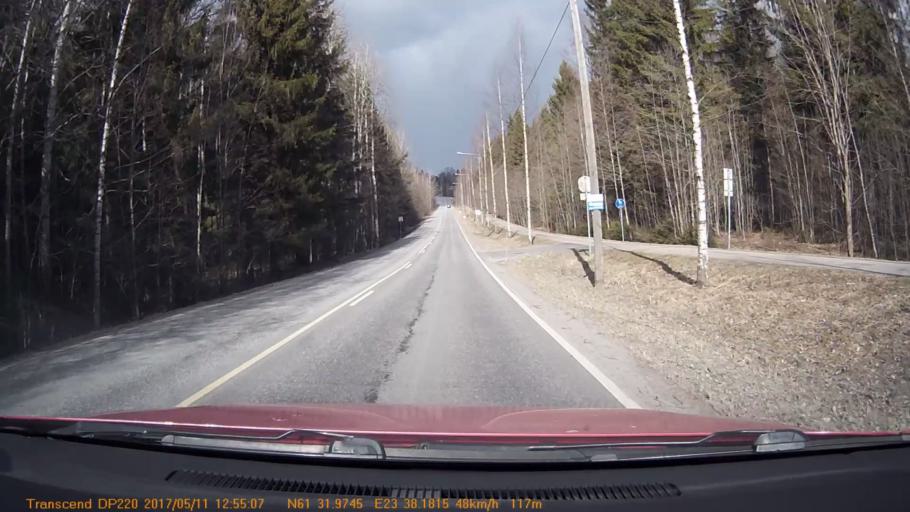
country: FI
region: Pirkanmaa
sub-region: Tampere
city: Yloejaervi
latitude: 61.5329
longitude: 23.6364
